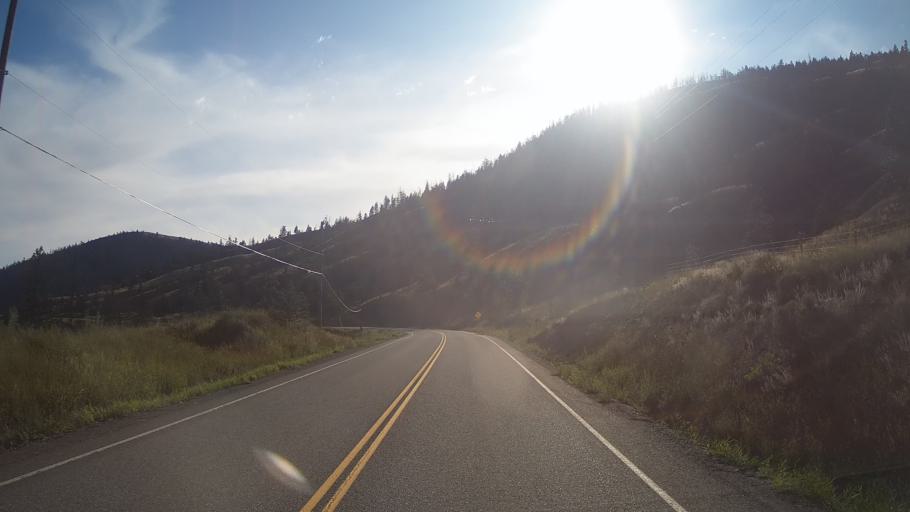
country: CA
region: British Columbia
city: Cache Creek
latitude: 50.8827
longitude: -121.5037
